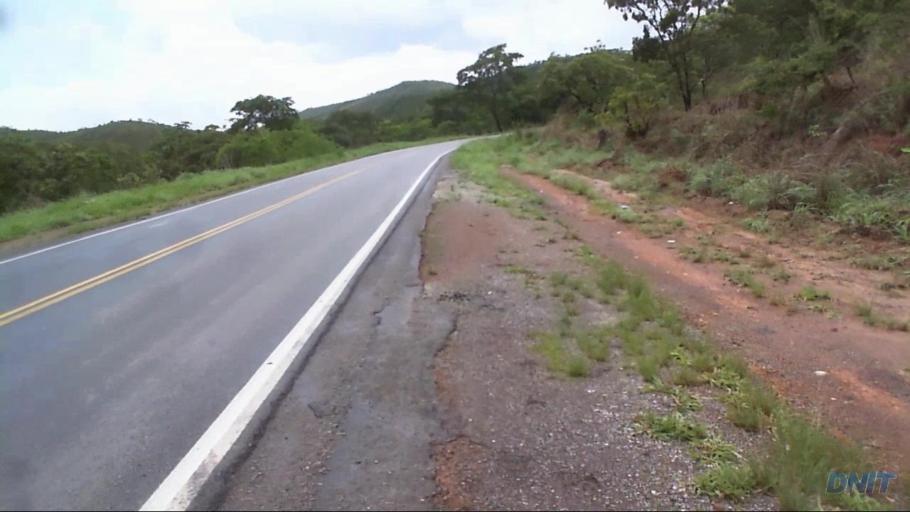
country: BR
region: Goias
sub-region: Padre Bernardo
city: Padre Bernardo
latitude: -15.4939
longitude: -48.2248
